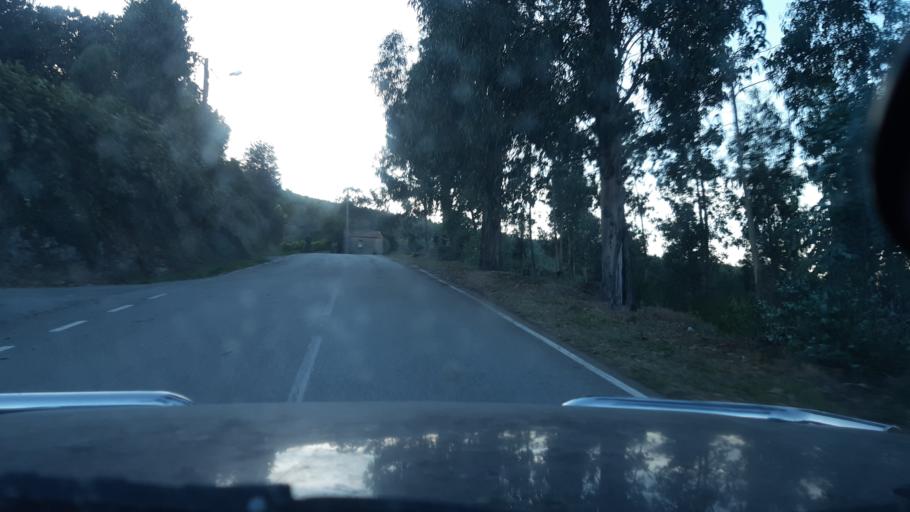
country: PT
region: Aveiro
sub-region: Agueda
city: Aguada de Cima
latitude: 40.5436
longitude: -8.2763
